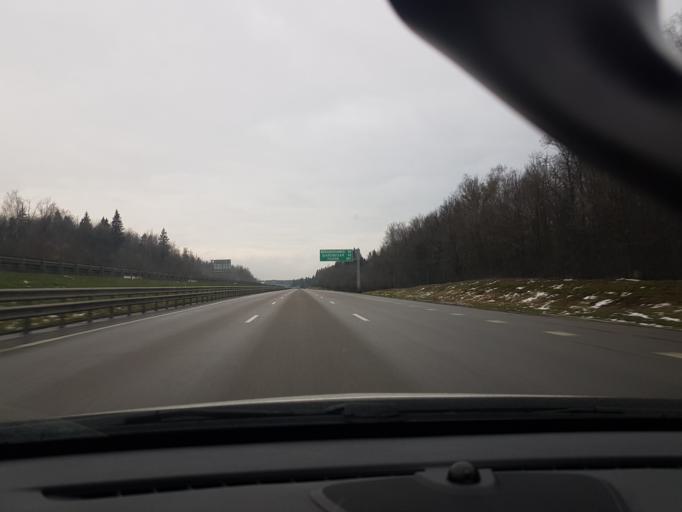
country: RU
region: Moskovskaya
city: Rumyantsevo
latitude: 55.9647
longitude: 36.5008
